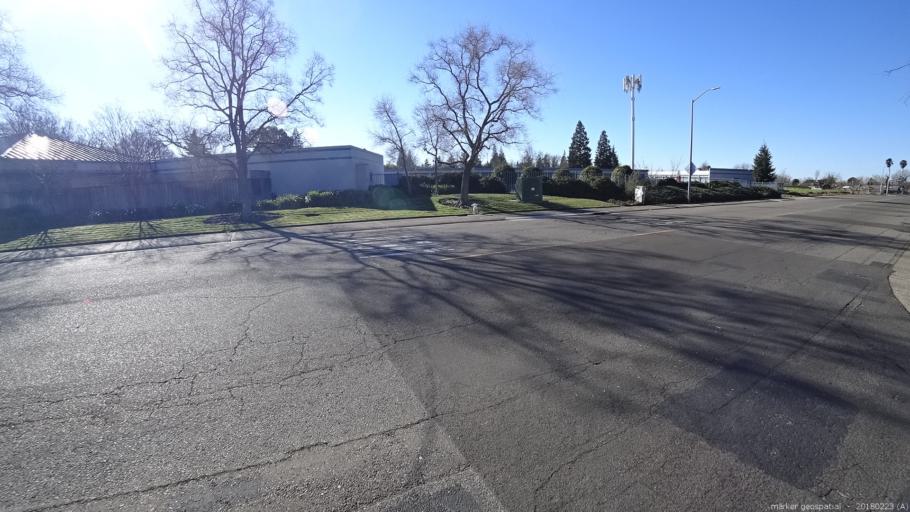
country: US
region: California
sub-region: Sacramento County
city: North Highlands
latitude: 38.7083
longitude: -121.3815
